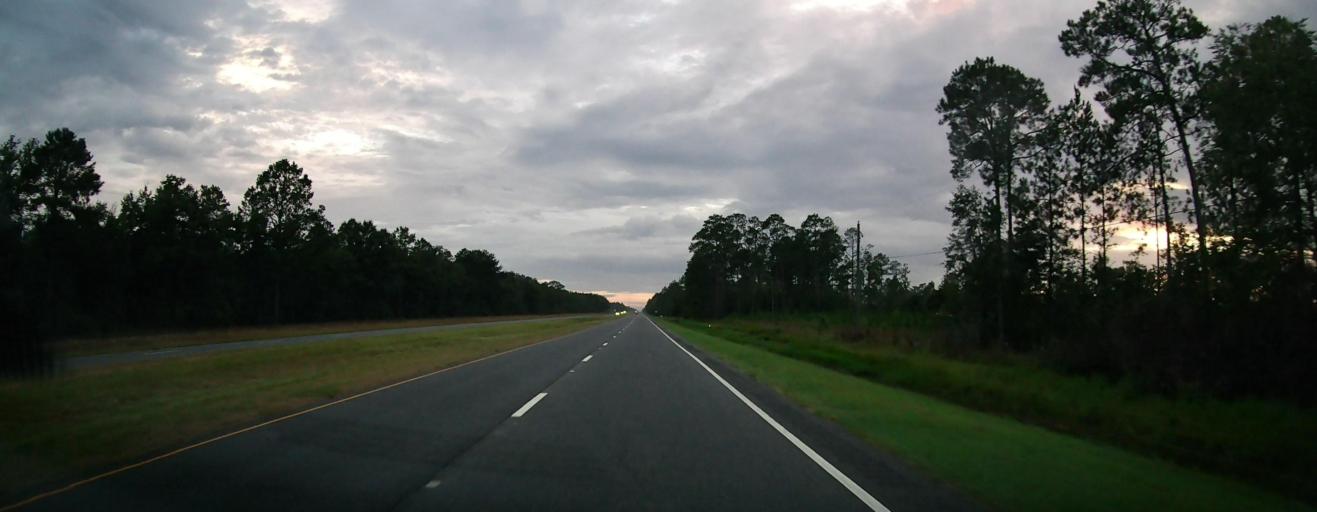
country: US
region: Georgia
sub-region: Lanier County
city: Lakeland
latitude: 30.8908
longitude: -83.1236
